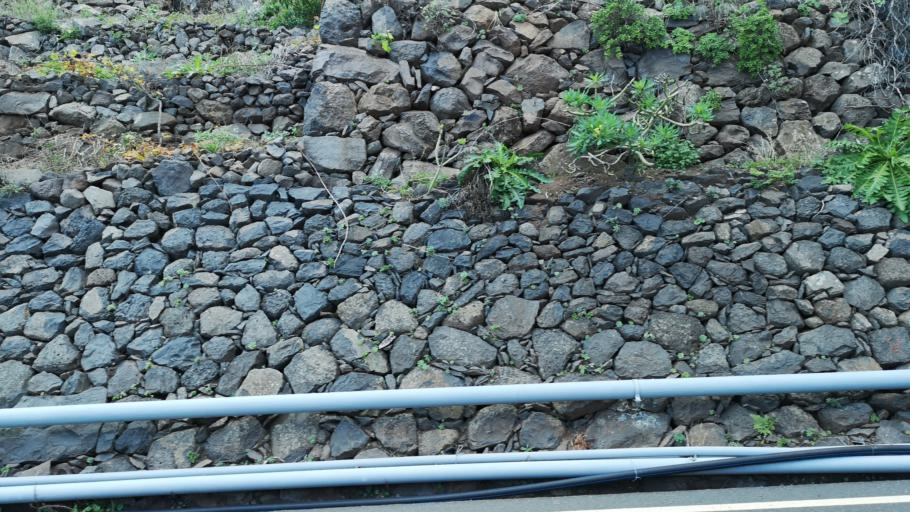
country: ES
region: Canary Islands
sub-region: Provincia de Santa Cruz de Tenerife
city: Agulo
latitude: 28.1855
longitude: -17.1969
